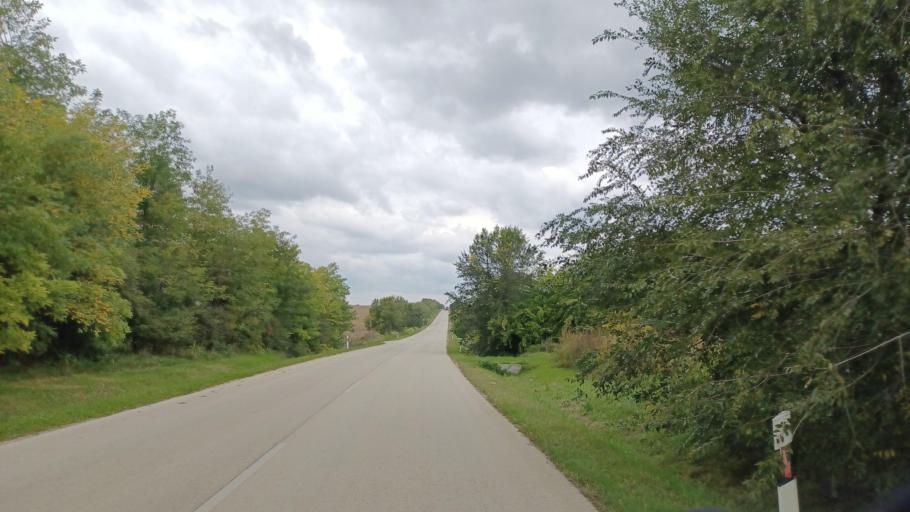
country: HU
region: Tolna
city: Simontornya
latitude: 46.7306
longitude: 18.5691
